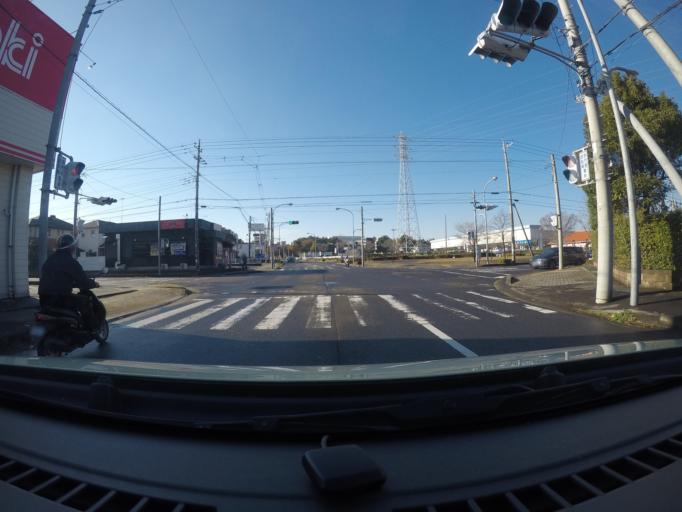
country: JP
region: Ibaraki
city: Tsukuba
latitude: 36.1311
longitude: 140.0802
